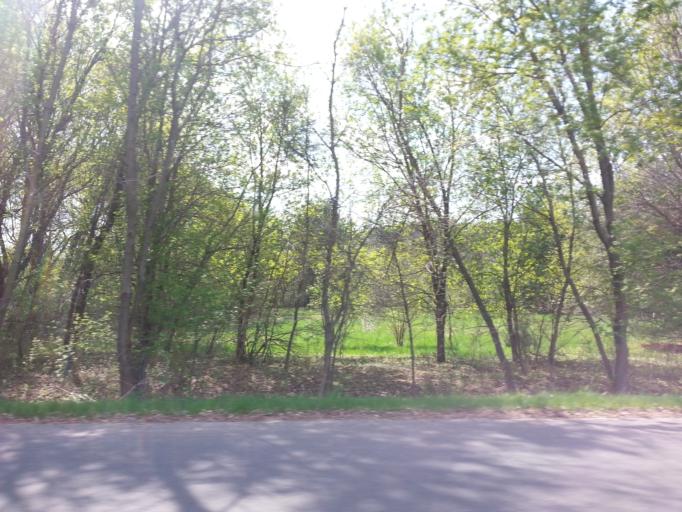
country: US
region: Minnesota
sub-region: Washington County
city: Lake Elmo
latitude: 44.9856
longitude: -92.8306
